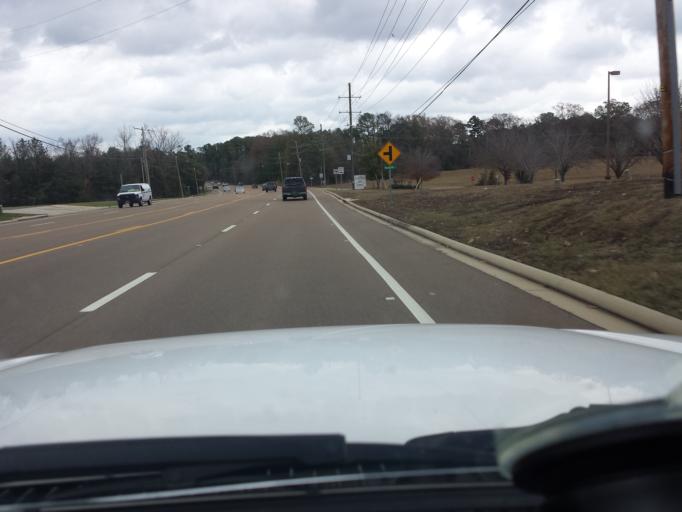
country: US
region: Mississippi
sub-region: Rankin County
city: Flowood
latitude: 32.3583
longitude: -90.0592
